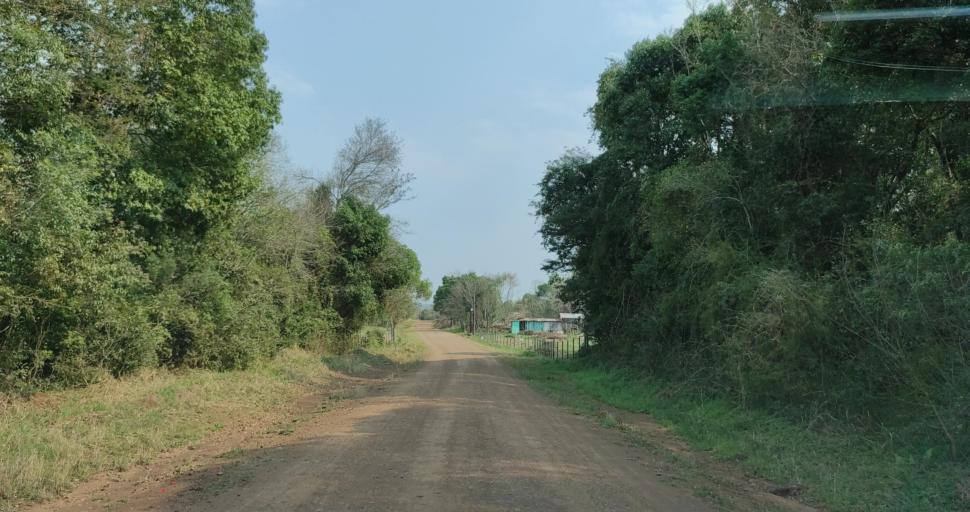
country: AR
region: Misiones
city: Cerro Cora
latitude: -27.5575
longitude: -55.5795
